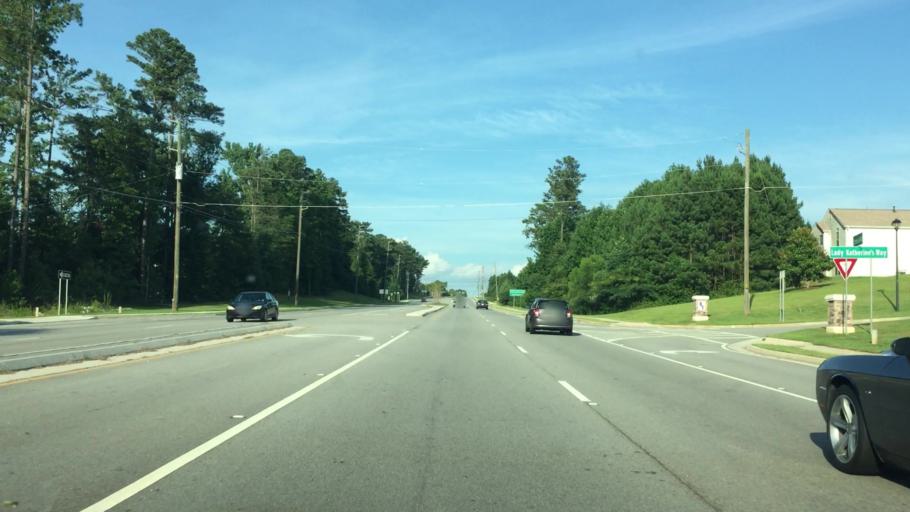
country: US
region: Georgia
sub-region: Clayton County
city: Lake City
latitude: 33.6103
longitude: -84.2777
